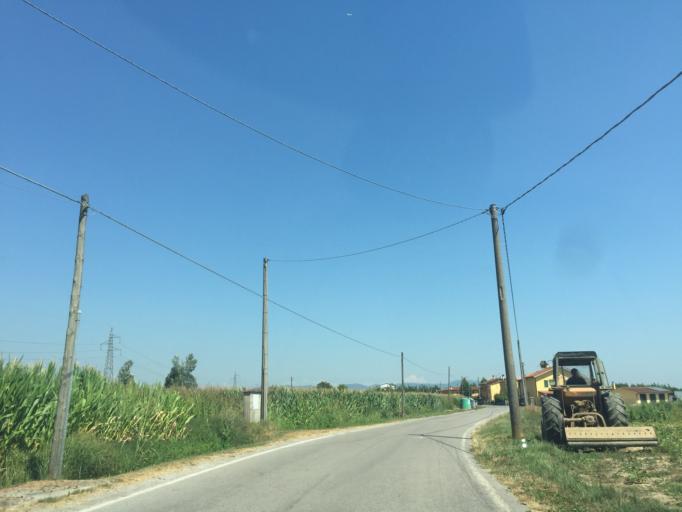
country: IT
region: Tuscany
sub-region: Provincia di Pistoia
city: Ponte Buggianese
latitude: 43.8338
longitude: 10.7377
